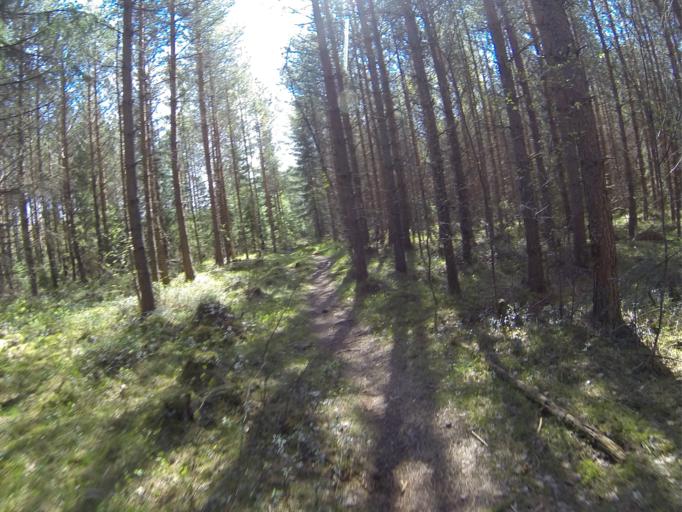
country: FI
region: Varsinais-Suomi
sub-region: Salo
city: Pertteli
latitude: 60.3936
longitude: 23.2075
